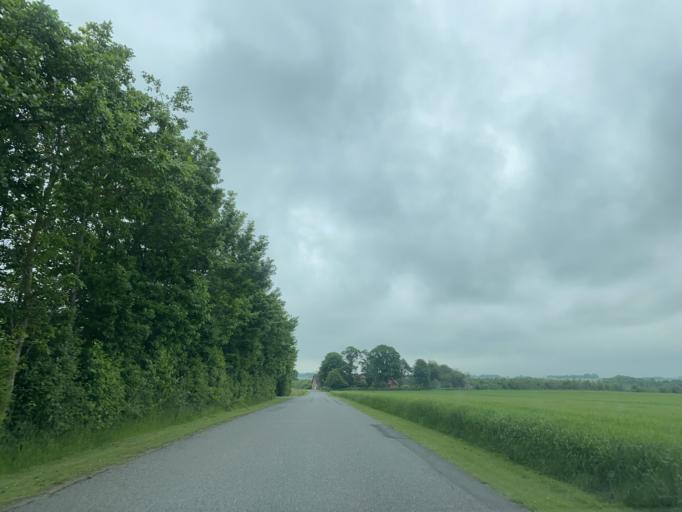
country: DK
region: Central Jutland
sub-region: Viborg Kommune
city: Bjerringbro
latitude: 56.3374
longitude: 9.6543
